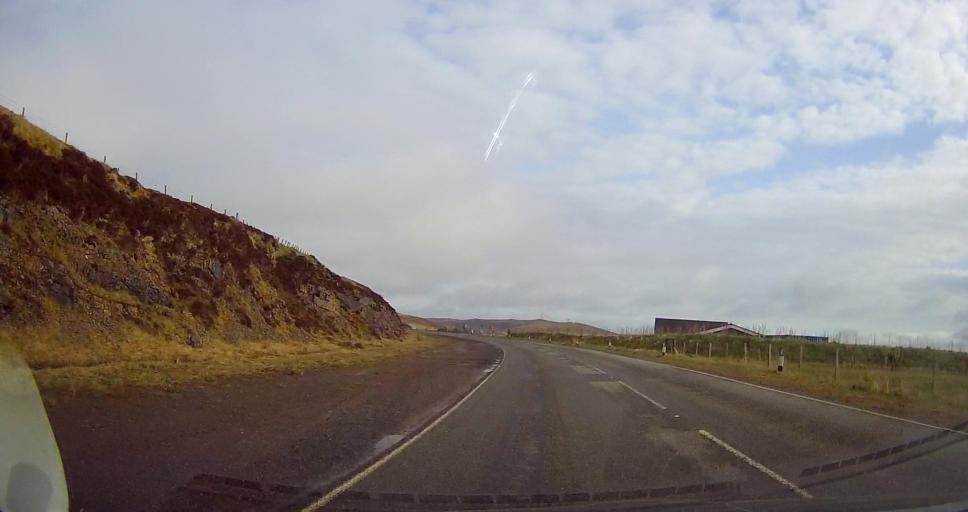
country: GB
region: Scotland
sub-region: Shetland Islands
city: Lerwick
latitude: 60.1192
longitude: -1.2154
